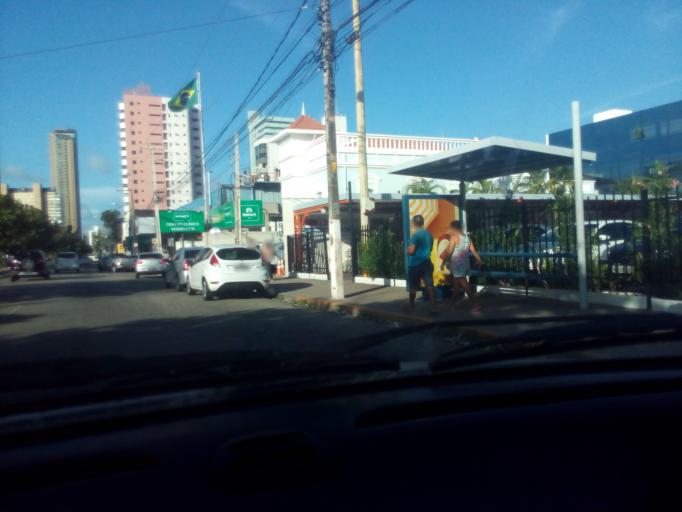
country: BR
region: Rio Grande do Norte
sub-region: Natal
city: Natal
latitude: -5.7849
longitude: -35.2032
